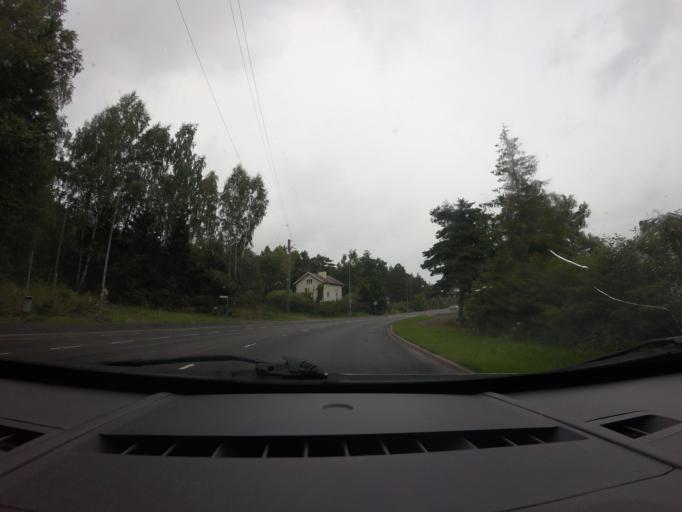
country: FI
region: Varsinais-Suomi
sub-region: Turku
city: Turku
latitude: 60.4245
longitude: 22.2921
